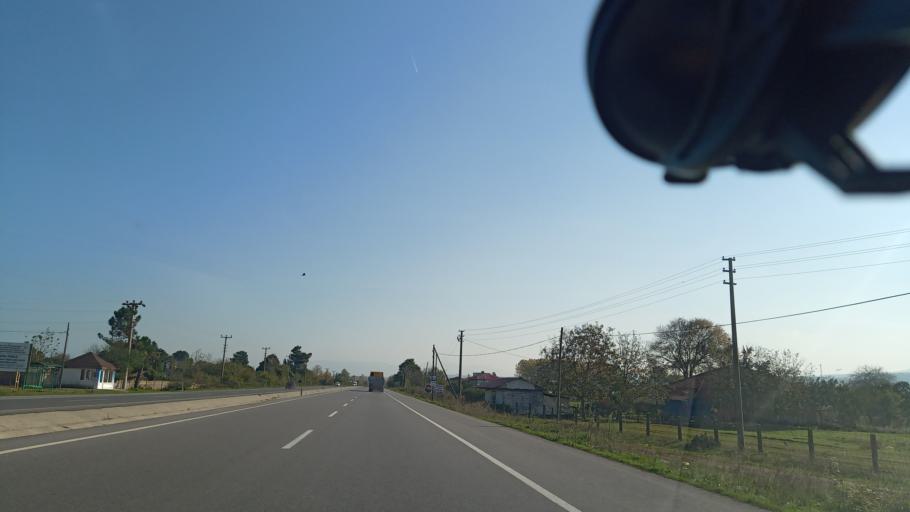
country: TR
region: Sakarya
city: Karasu
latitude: 41.0795
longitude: 30.7716
